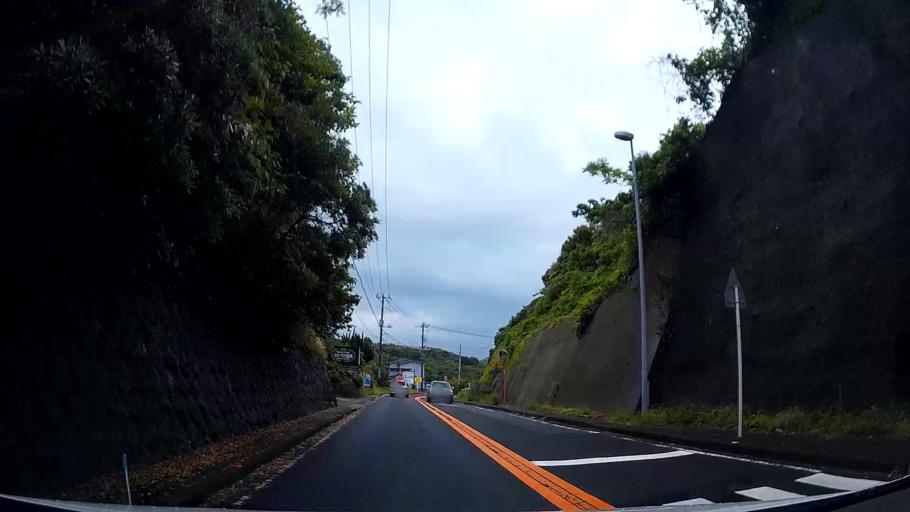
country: JP
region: Shizuoka
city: Shimoda
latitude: 34.6833
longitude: 138.9760
